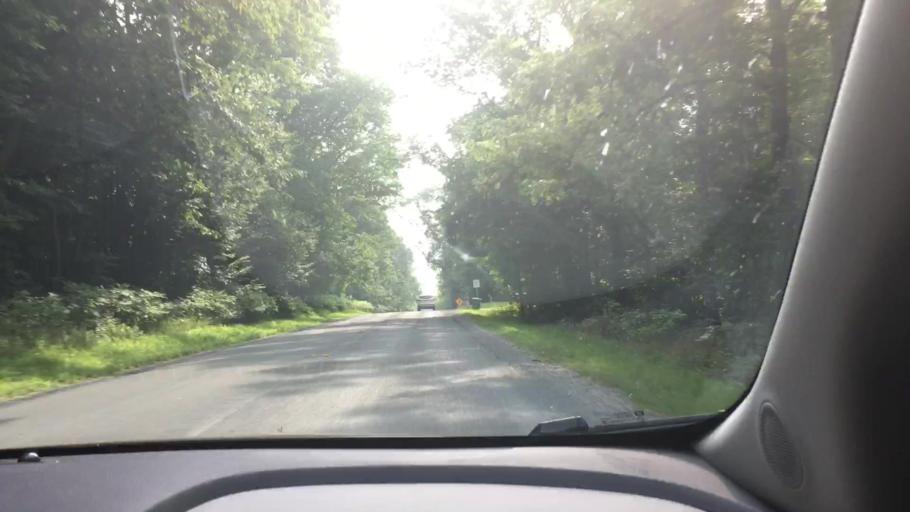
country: US
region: Michigan
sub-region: Cass County
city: Marcellus
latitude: 42.0273
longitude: -85.7067
